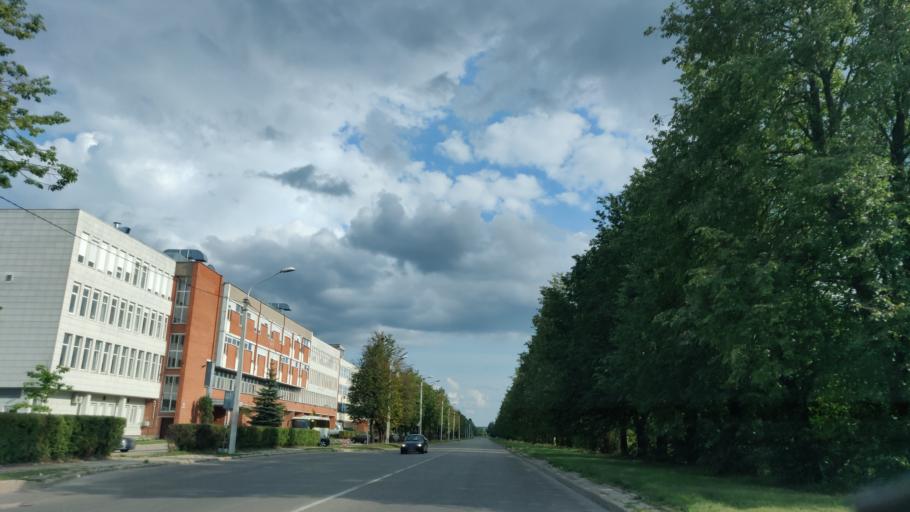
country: LT
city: Baltoji Voke
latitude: 54.6250
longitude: 25.1404
